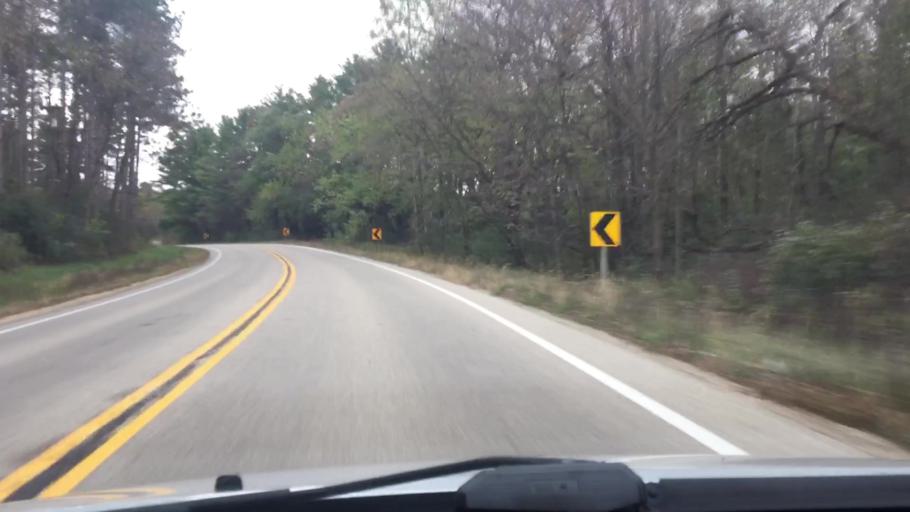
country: US
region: Wisconsin
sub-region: Waukesha County
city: Eagle
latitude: 42.9182
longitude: -88.4733
